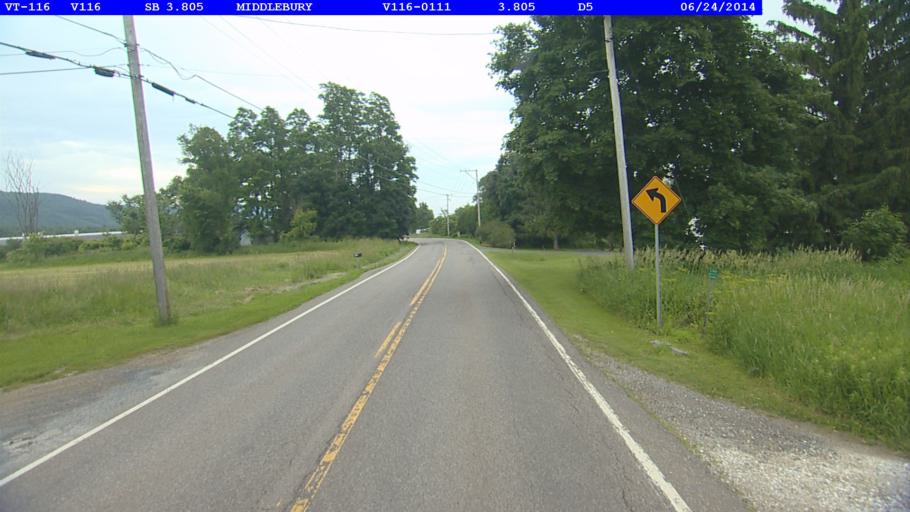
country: US
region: Vermont
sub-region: Addison County
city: Middlebury (village)
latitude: 44.0172
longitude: -73.1025
